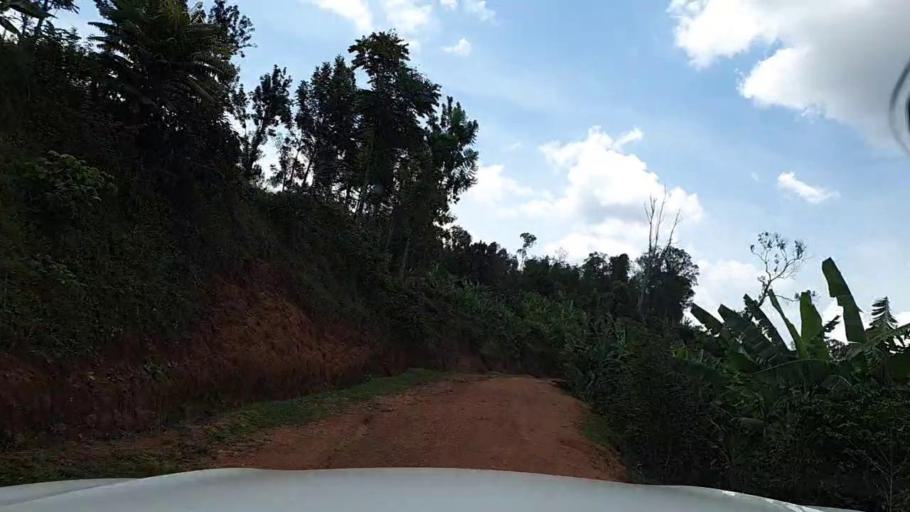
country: RW
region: Southern Province
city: Butare
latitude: -2.7522
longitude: 29.7609
